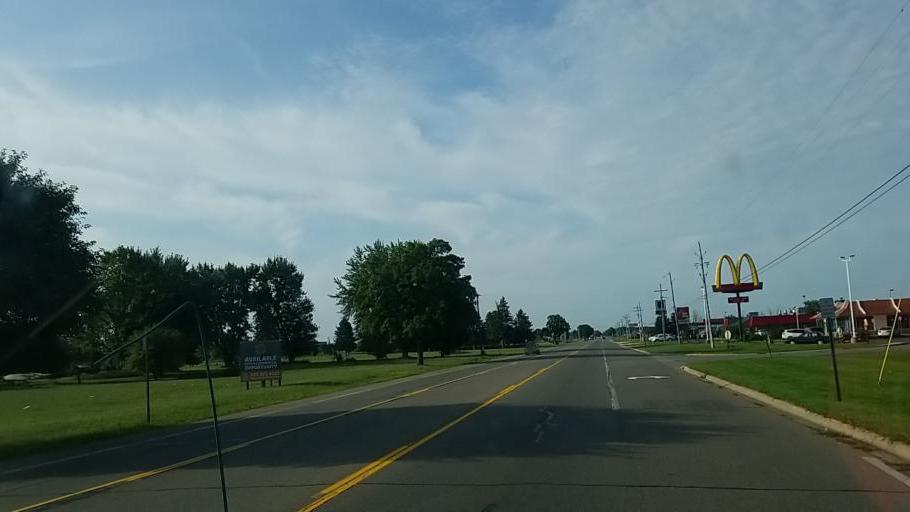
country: US
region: Michigan
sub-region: Ionia County
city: Ionia
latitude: 42.9474
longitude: -85.0748
